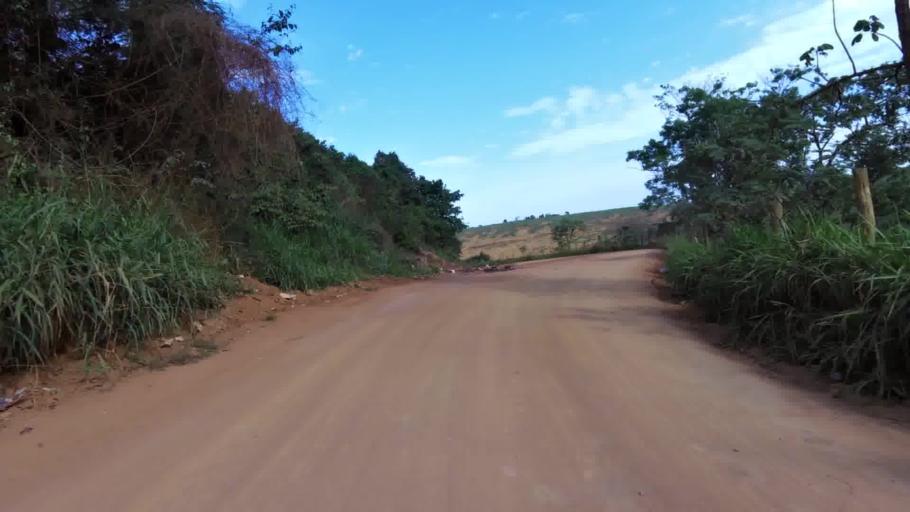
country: BR
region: Espirito Santo
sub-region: Piuma
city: Piuma
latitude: -20.8340
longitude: -40.7381
